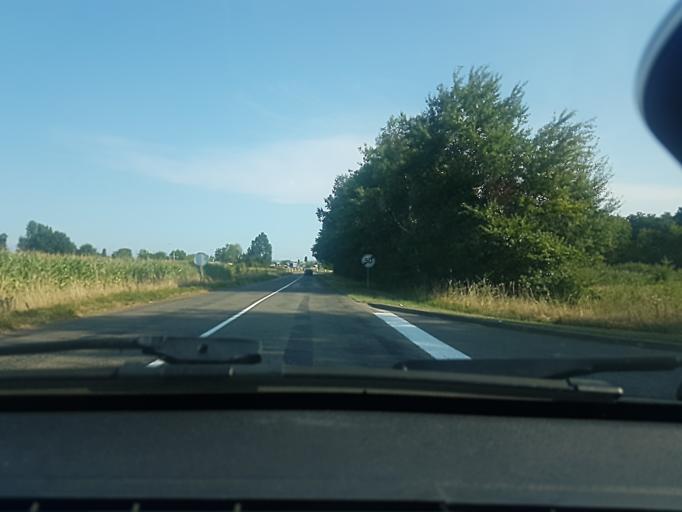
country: FR
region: Bourgogne
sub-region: Departement de Saone-et-Loire
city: Varennes-le-Grand
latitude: 46.6978
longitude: 4.8416
